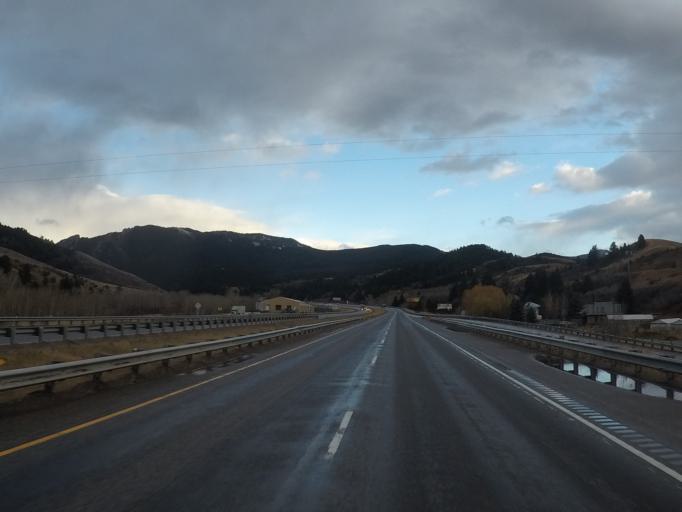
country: US
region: Montana
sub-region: Gallatin County
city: Bozeman
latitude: 45.6533
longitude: -110.9446
